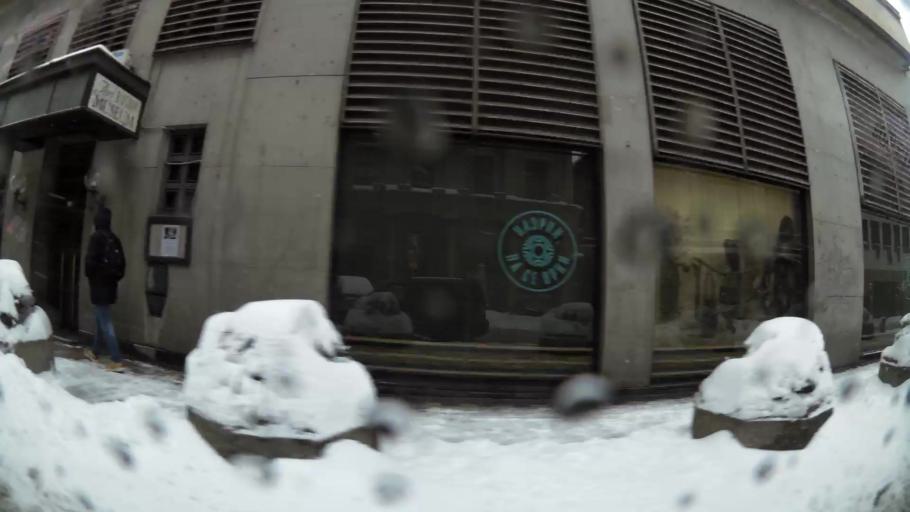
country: RS
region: Central Serbia
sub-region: Belgrade
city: Stari Grad
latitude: 44.8198
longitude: 20.4562
